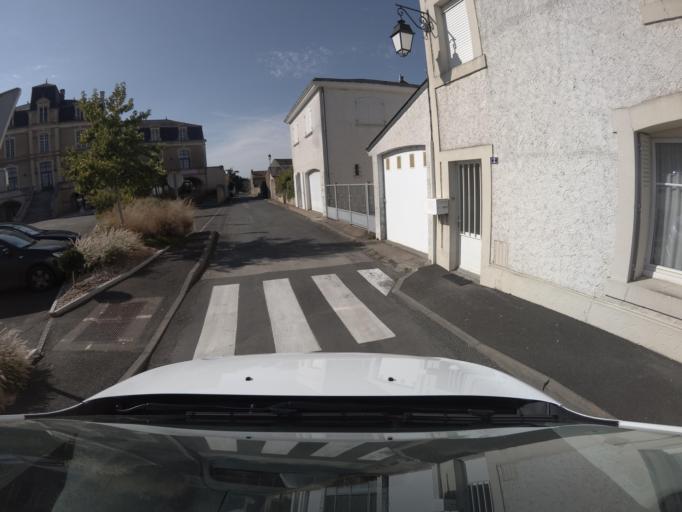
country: FR
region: Poitou-Charentes
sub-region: Departement des Deux-Sevres
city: Argenton-les-Vallees
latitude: 46.9855
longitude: -0.4497
